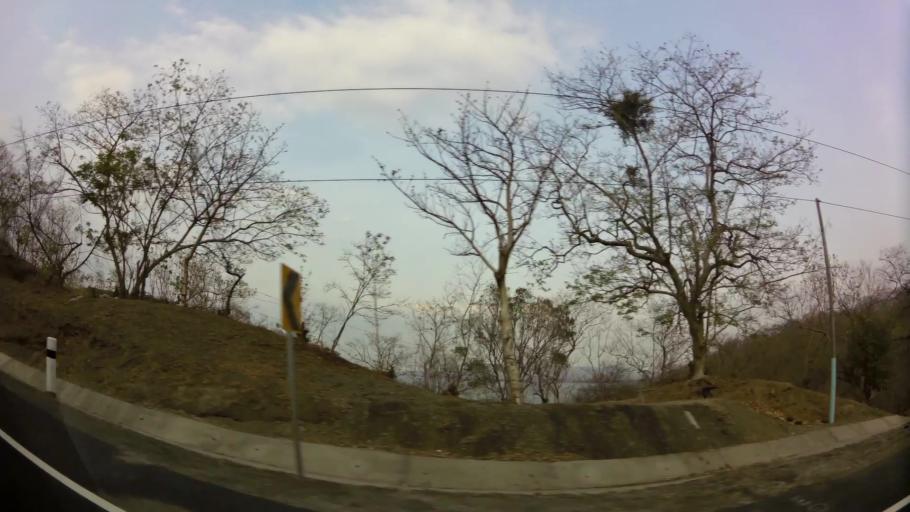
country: NI
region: Leon
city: Nagarote
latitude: 12.2486
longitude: -86.4458
